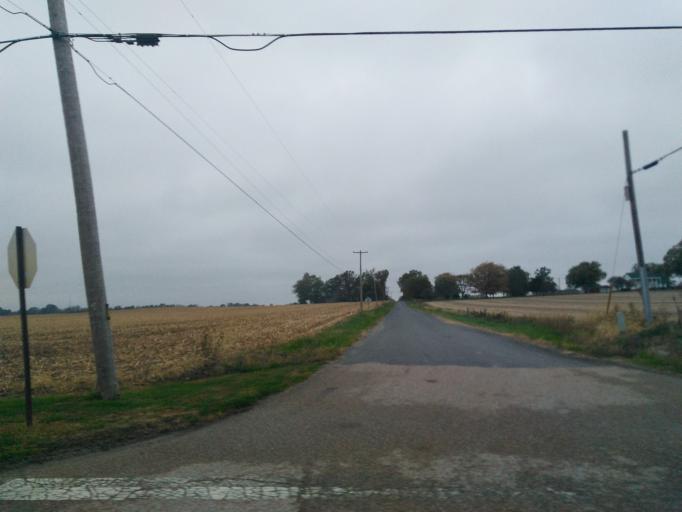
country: US
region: Illinois
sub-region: Bond County
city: Greenville
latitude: 38.8765
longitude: -89.4142
